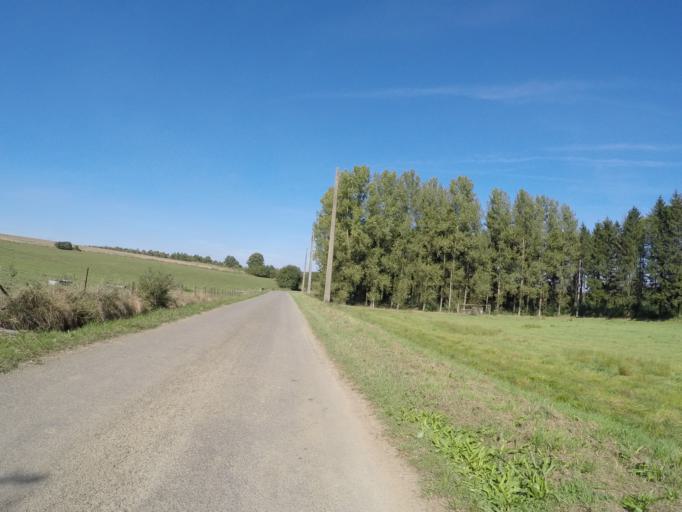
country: BE
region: Wallonia
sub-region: Province de Namur
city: Assesse
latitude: 50.3154
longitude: 5.0064
